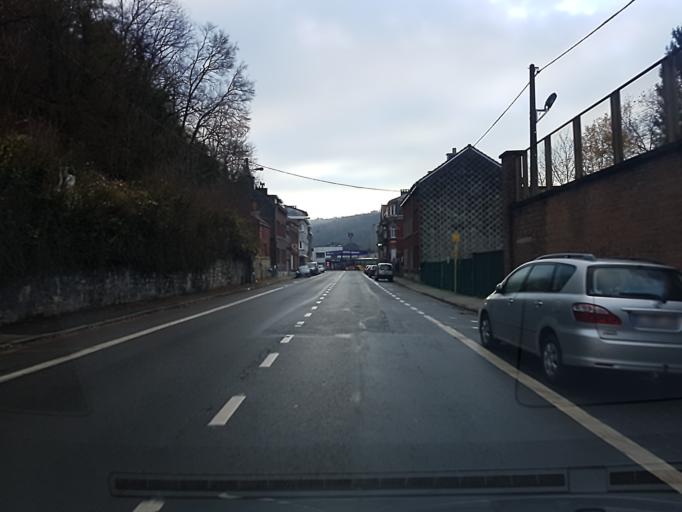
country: BE
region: Wallonia
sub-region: Province de Liege
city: Pepinster
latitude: 50.5700
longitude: 5.8017
